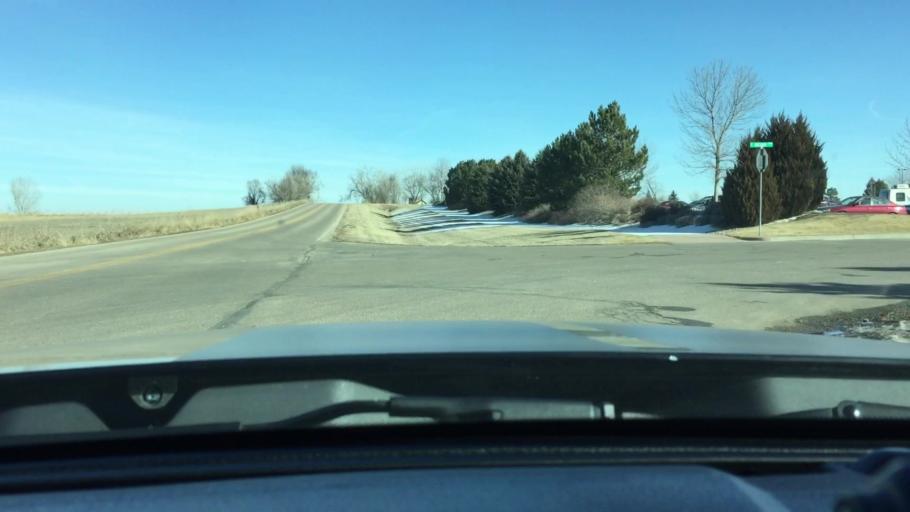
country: US
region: Colorado
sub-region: Weld County
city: Johnstown
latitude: 40.3636
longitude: -104.9772
